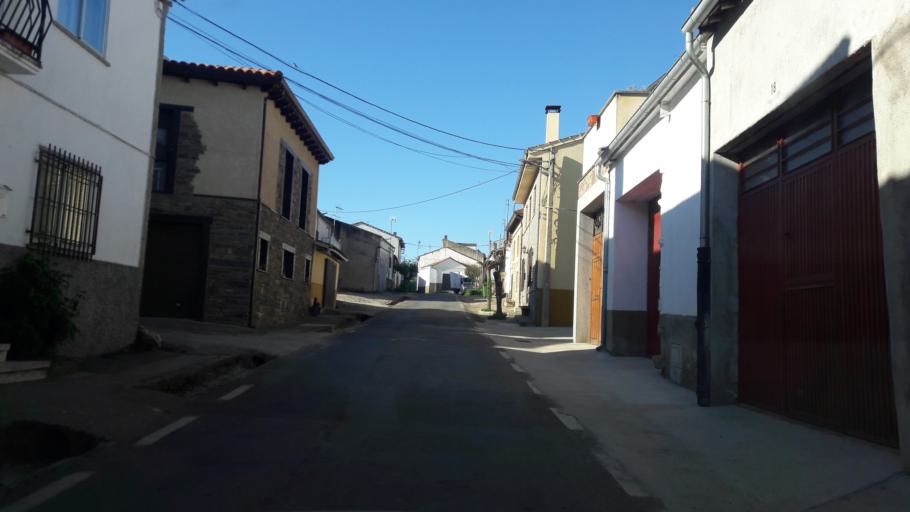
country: ES
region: Castille and Leon
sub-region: Provincia de Salamanca
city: Endrinal
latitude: 40.5915
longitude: -5.8035
